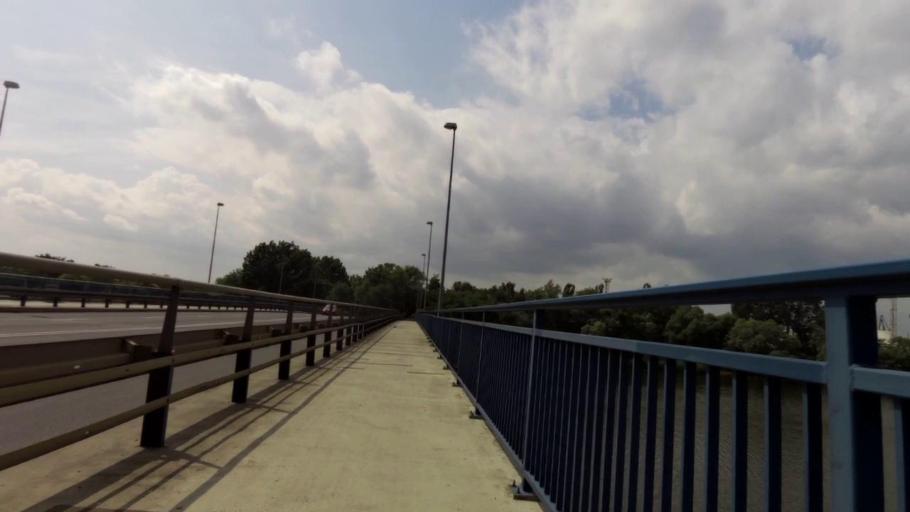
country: PL
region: West Pomeranian Voivodeship
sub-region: Szczecin
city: Szczecin
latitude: 53.3982
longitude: 14.6136
